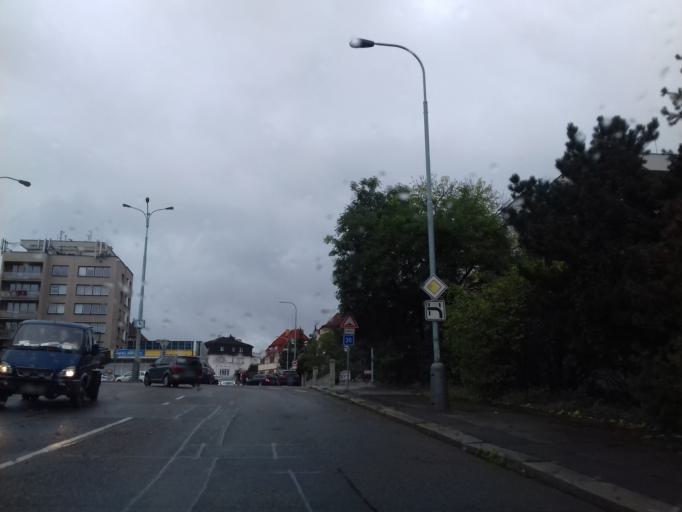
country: CZ
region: Praha
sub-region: Praha 1
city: Mala Strana
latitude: 50.0649
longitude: 14.3898
